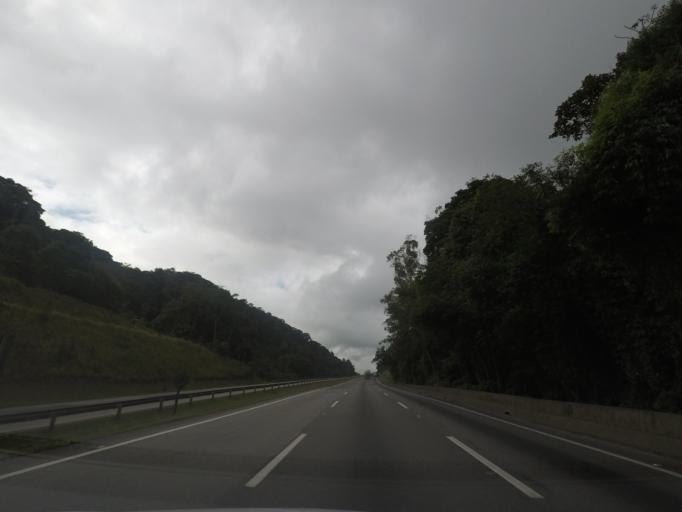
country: BR
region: Sao Paulo
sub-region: Juquitiba
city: Juquitiba
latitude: -24.0336
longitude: -47.1835
